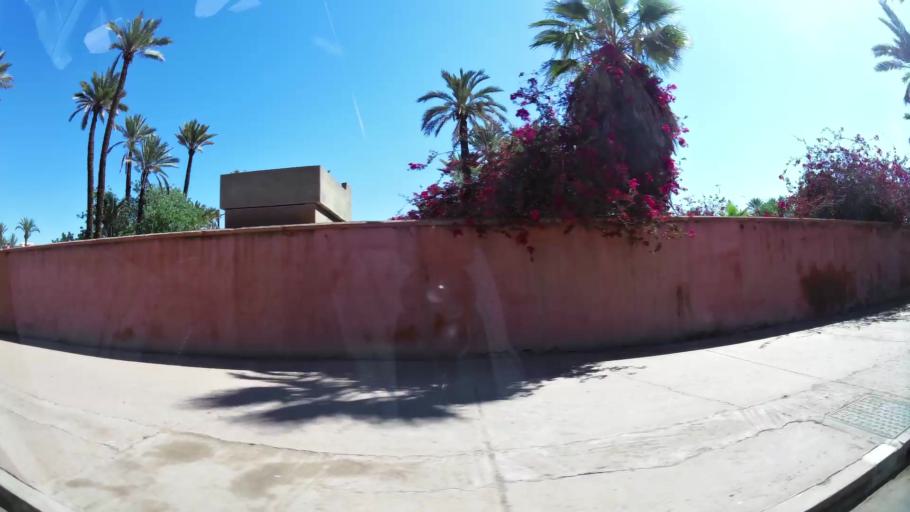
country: MA
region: Marrakech-Tensift-Al Haouz
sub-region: Marrakech
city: Marrakesh
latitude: 31.6400
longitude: -8.0100
